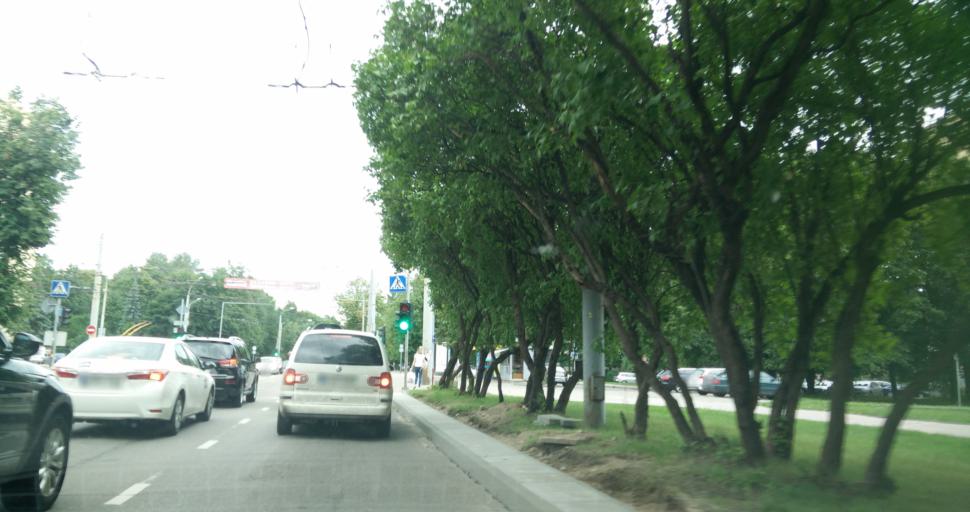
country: LT
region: Vilnius County
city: Rasos
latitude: 54.7122
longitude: 25.3149
